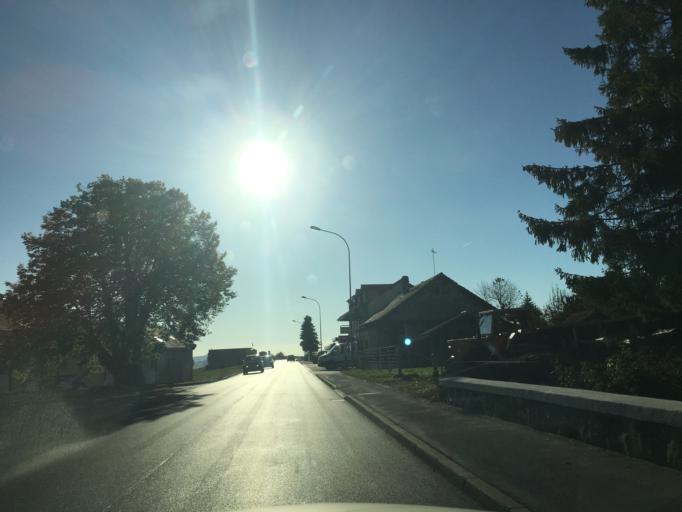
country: CH
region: Vaud
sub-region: Lavaux-Oron District
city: Oron-la-ville
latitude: 46.5767
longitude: 6.8686
